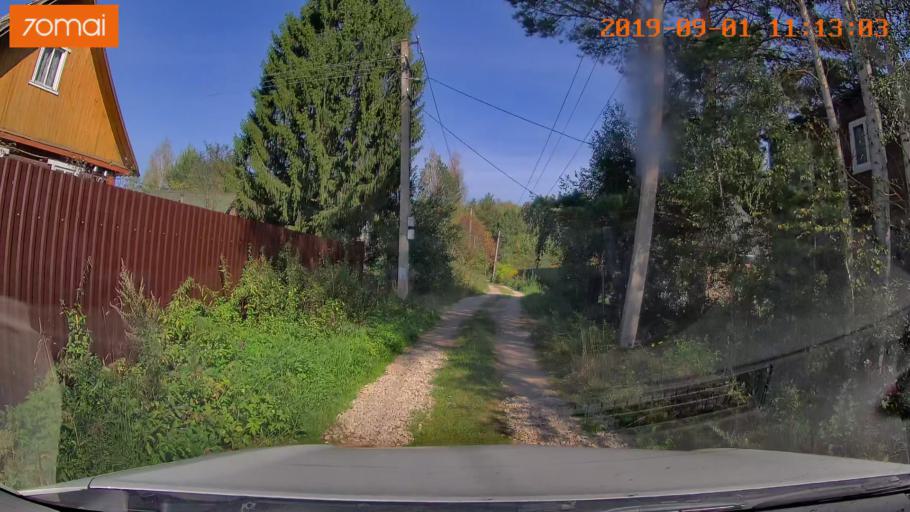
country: RU
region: Kaluga
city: Detchino
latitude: 54.8207
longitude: 36.3718
